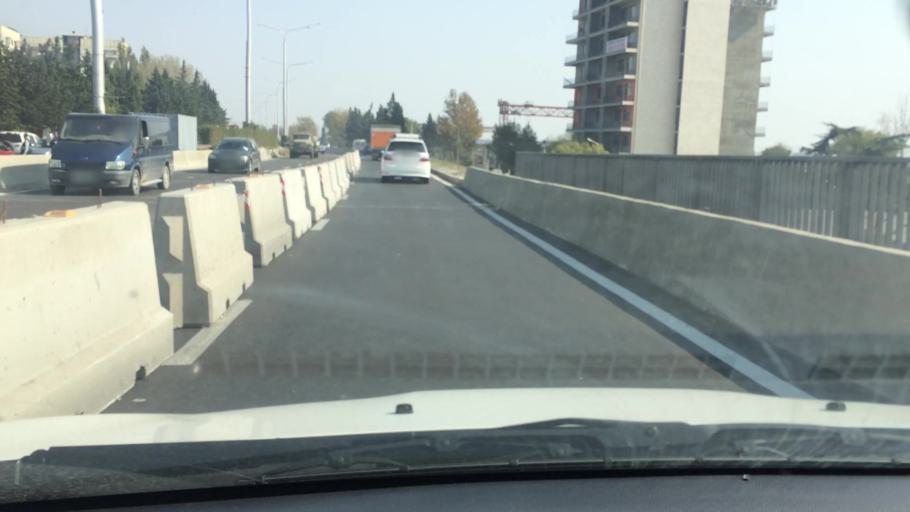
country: GE
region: T'bilisi
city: Tbilisi
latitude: 41.6841
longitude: 44.8705
